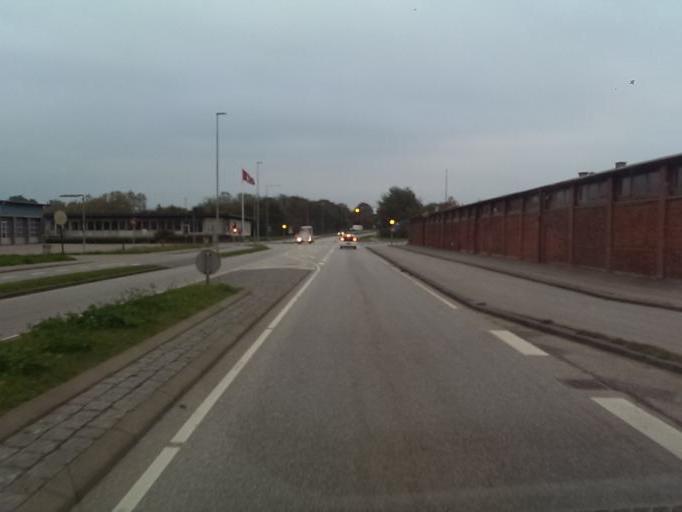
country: DK
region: South Denmark
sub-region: Esbjerg Kommune
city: Esbjerg
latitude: 55.4634
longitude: 8.4633
